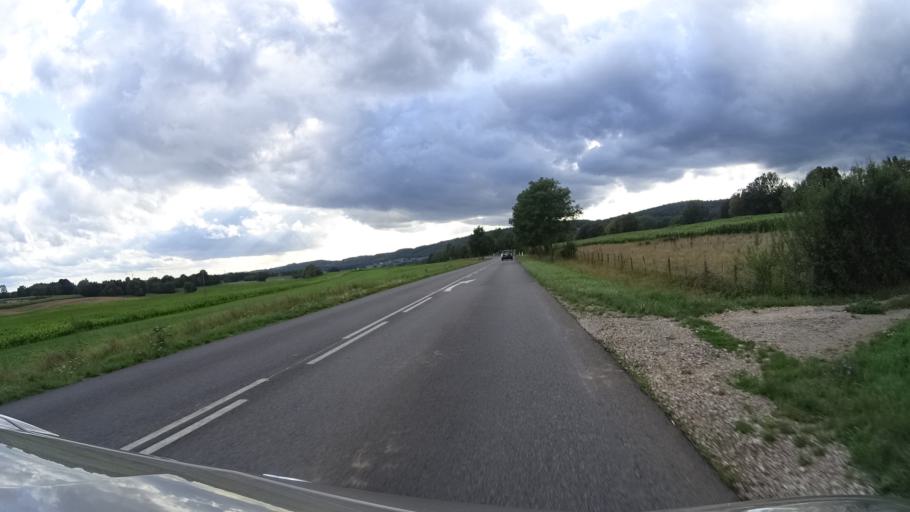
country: FR
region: Franche-Comte
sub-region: Departement du Doubs
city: Saone
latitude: 47.2429
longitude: 6.1391
